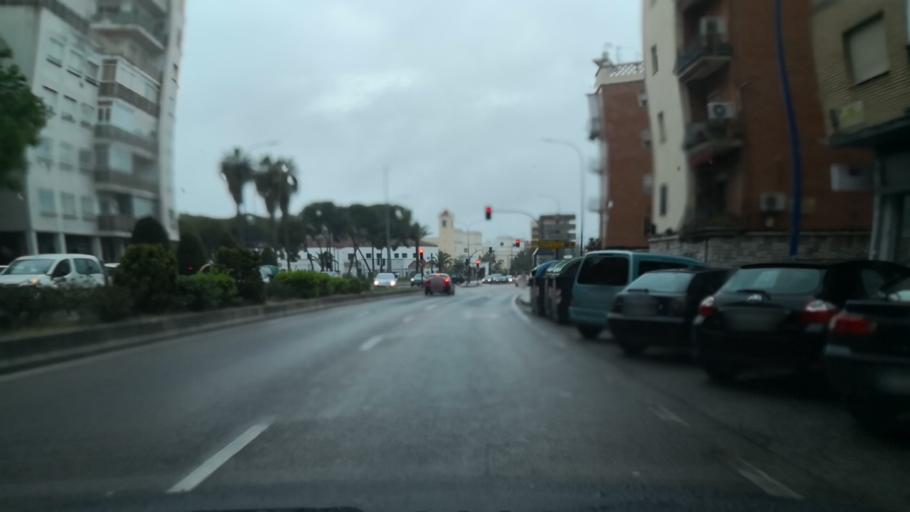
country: ES
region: Extremadura
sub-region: Provincia de Badajoz
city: Badajoz
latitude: 38.8701
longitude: -6.9775
